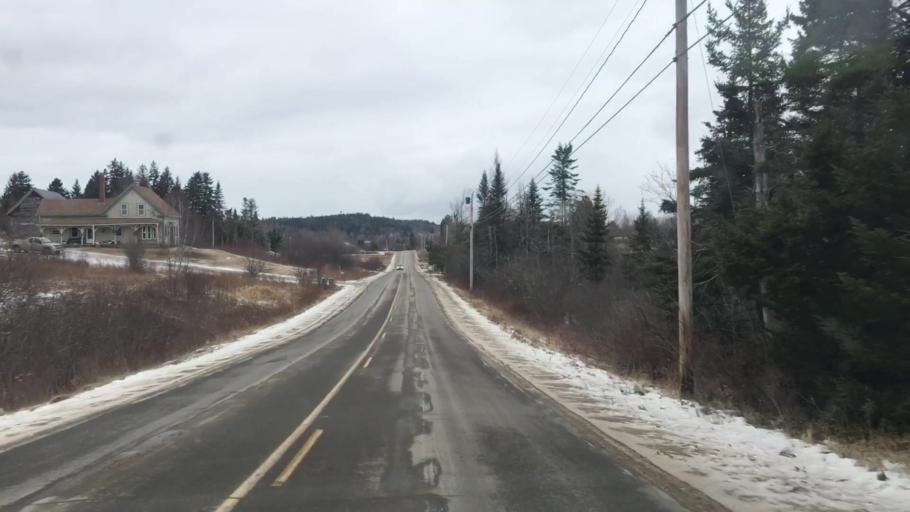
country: US
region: Maine
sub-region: Washington County
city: Machiasport
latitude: 44.7078
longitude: -67.4026
